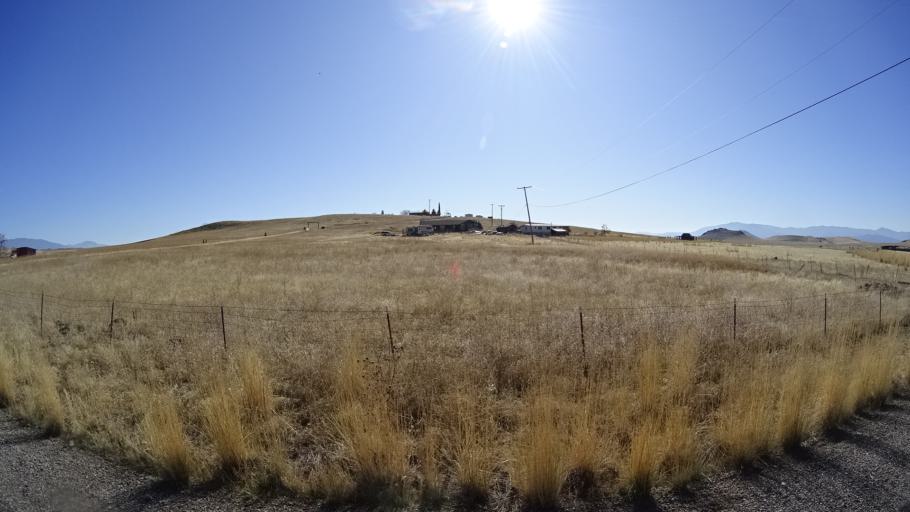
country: US
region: California
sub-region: Siskiyou County
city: Montague
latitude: 41.7559
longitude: -122.4688
